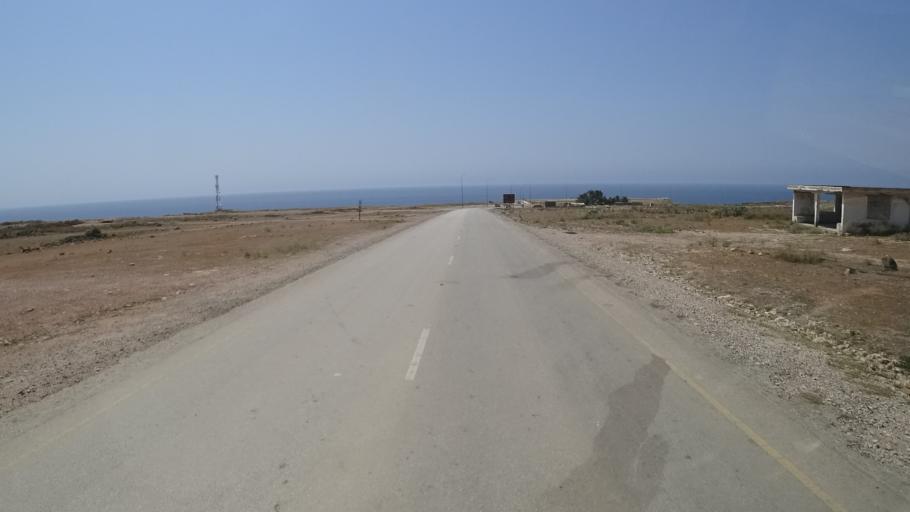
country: OM
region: Zufar
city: Salalah
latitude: 17.0359
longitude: 54.6127
